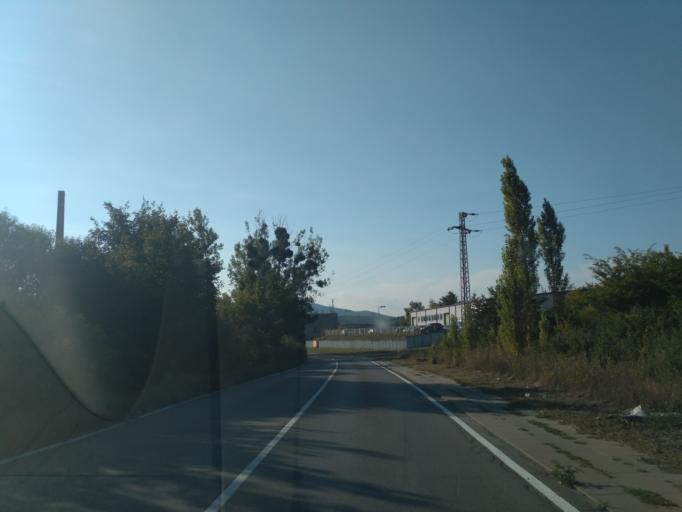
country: SK
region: Kosicky
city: Kosice
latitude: 48.7479
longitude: 21.2671
